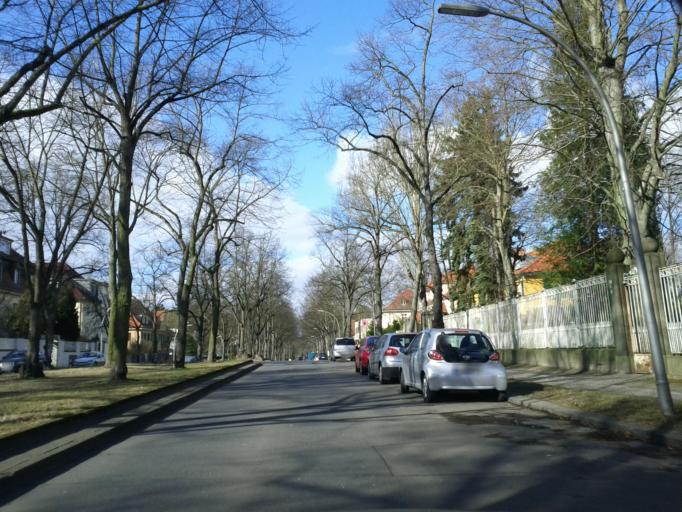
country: DE
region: Berlin
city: Schmargendorf
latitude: 52.4657
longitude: 13.2953
